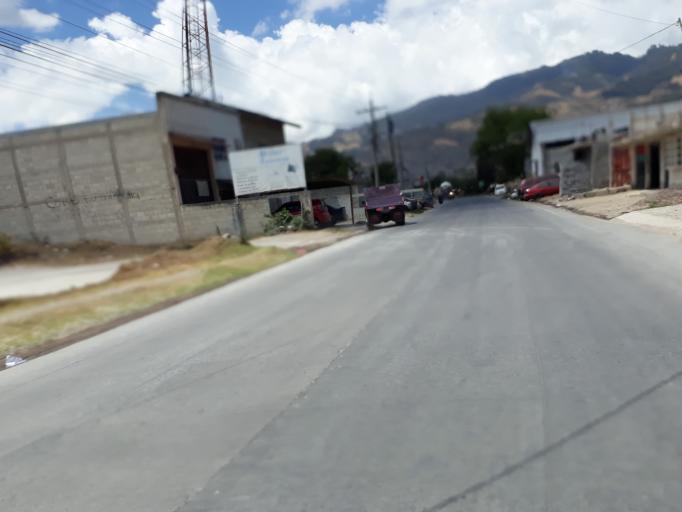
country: GT
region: Quetzaltenango
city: Quetzaltenango
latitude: 14.8206
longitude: -91.5384
